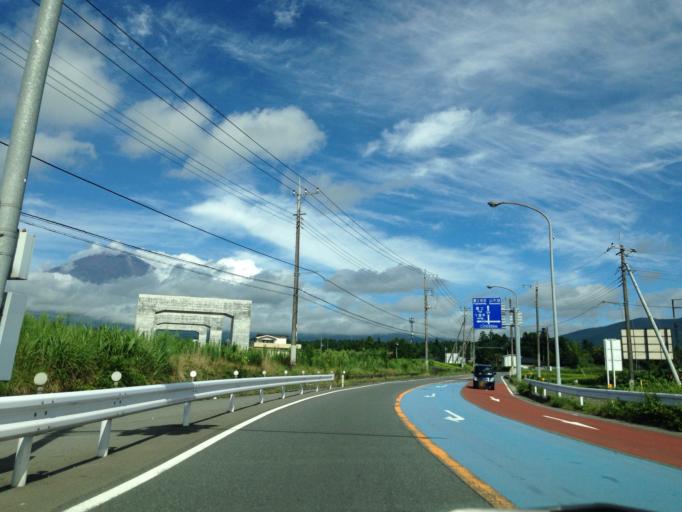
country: JP
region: Shizuoka
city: Gotemba
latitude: 35.3191
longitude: 138.9145
